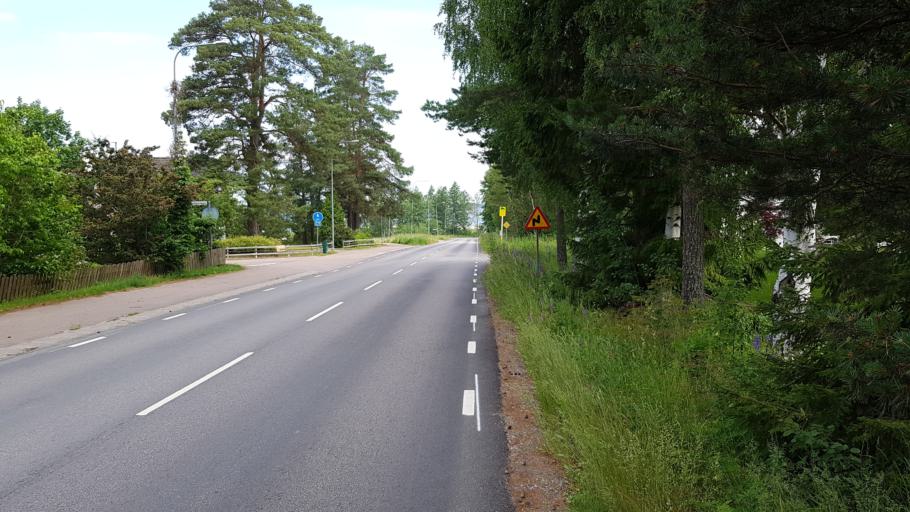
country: SE
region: Vaermland
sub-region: Karlstads Kommun
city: Karlstad
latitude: 59.3342
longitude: 13.5456
